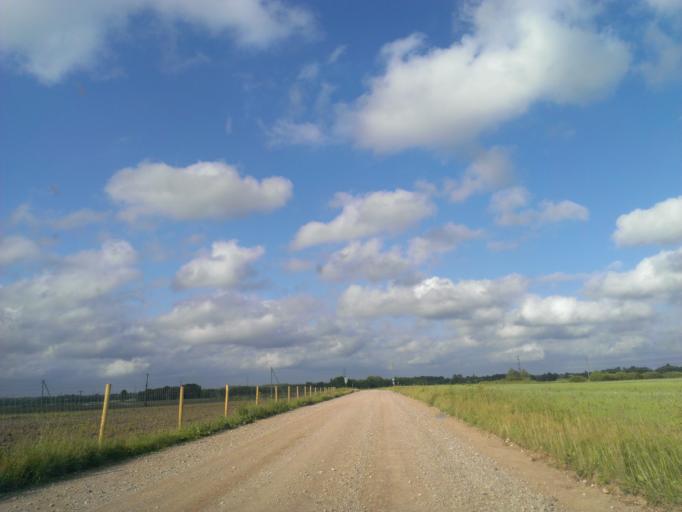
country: LV
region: Aizpute
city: Aizpute
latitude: 56.7712
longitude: 21.4710
